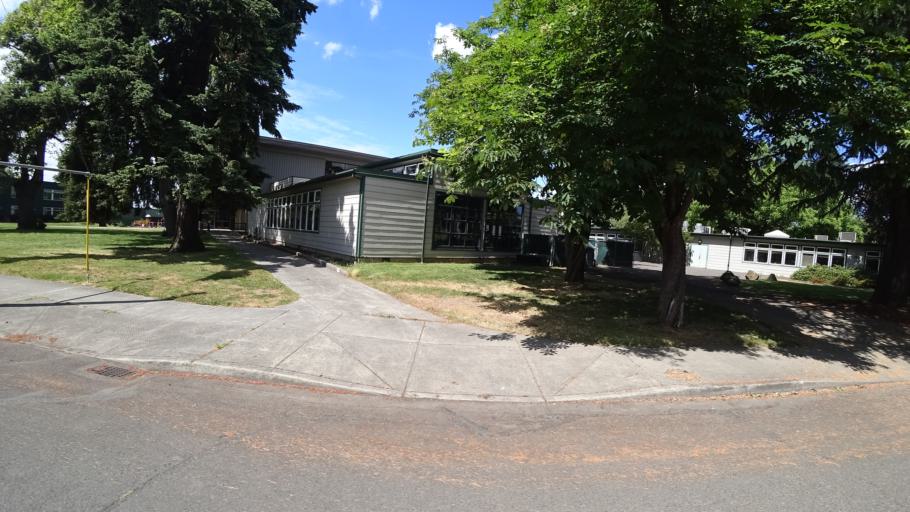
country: US
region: Washington
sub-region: Clark County
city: Vancouver
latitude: 45.5871
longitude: -122.7114
